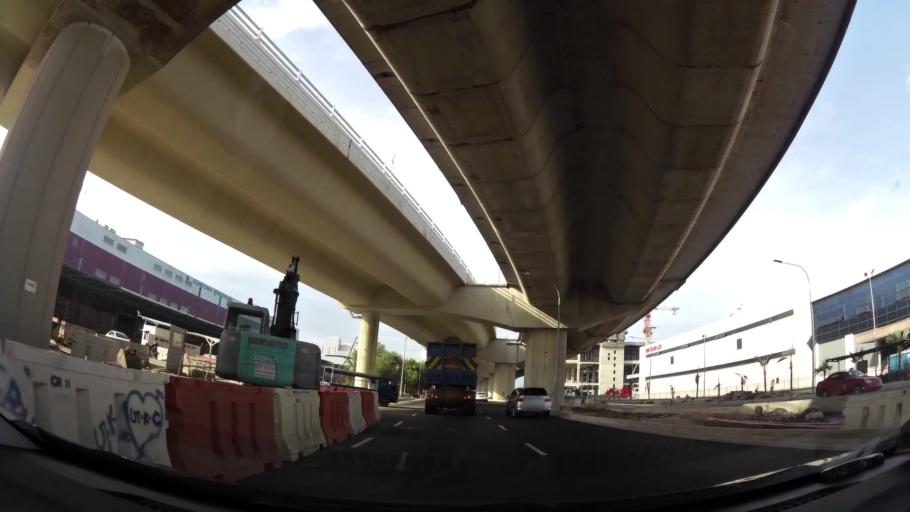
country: MY
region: Johor
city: Johor Bahru
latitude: 1.3292
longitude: 103.6375
